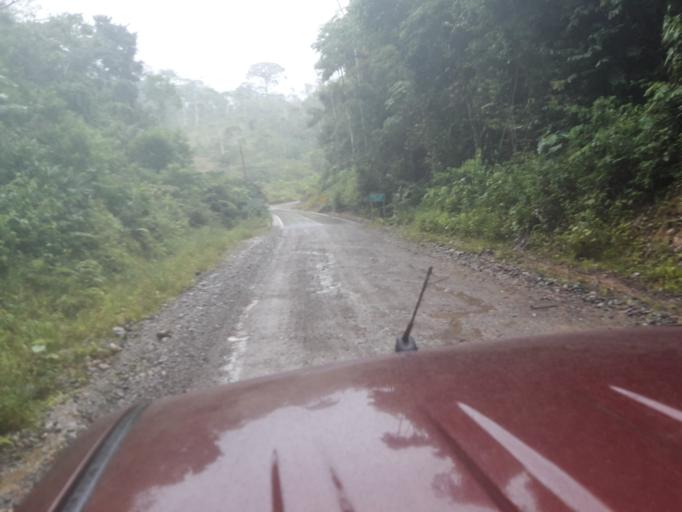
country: EC
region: Napo
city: Tena
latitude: -1.0246
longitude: -77.6626
